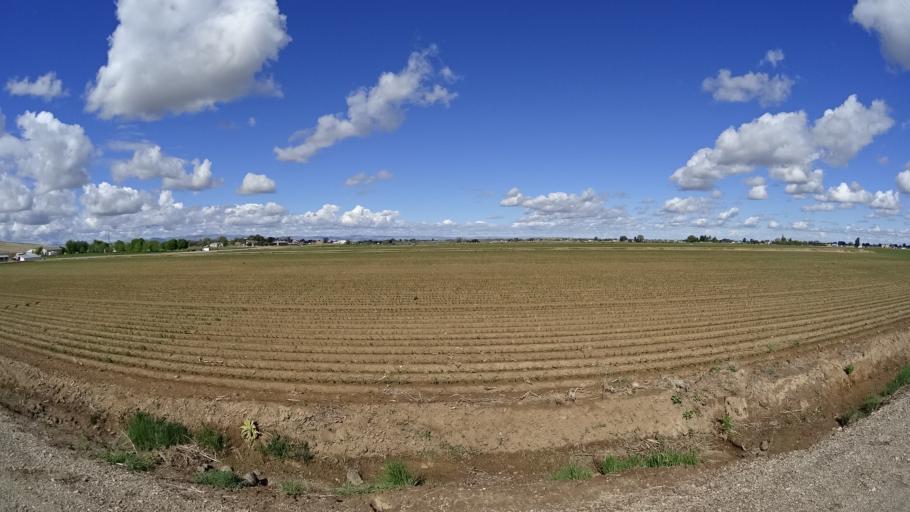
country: US
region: Idaho
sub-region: Ada County
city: Kuna
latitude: 43.4679
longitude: -116.4536
